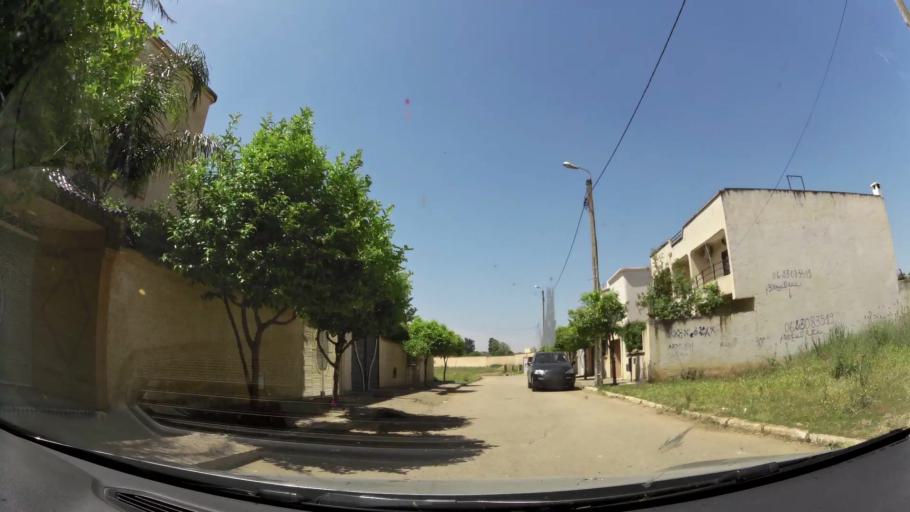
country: MA
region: Rabat-Sale-Zemmour-Zaer
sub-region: Khemisset
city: Khemisset
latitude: 33.8130
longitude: -6.0777
